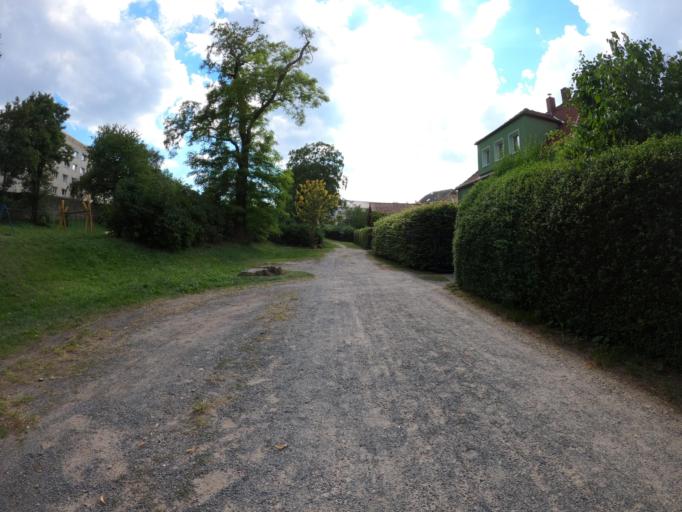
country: DE
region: Mecklenburg-Vorpommern
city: Woldegk
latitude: 53.4616
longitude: 13.5824
